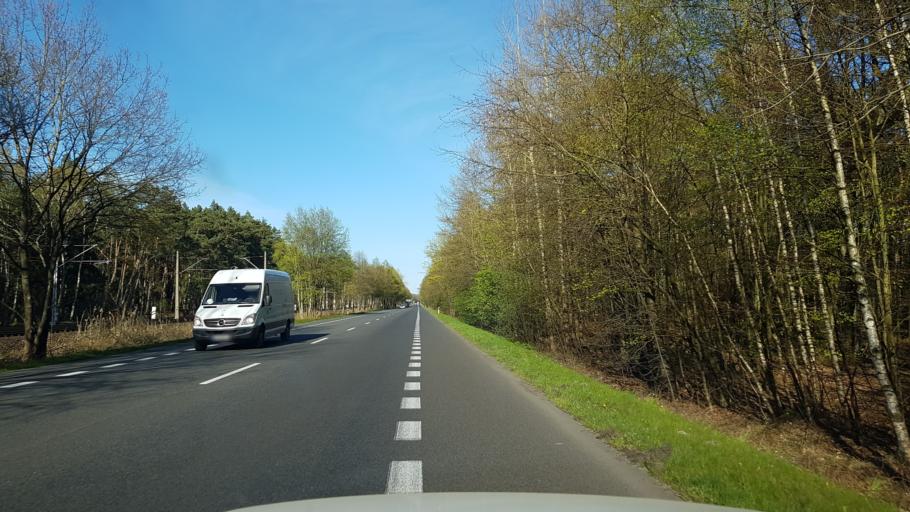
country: PL
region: West Pomeranian Voivodeship
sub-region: Powiat kamienski
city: Miedzyzdroje
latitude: 53.9047
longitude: 14.3816
